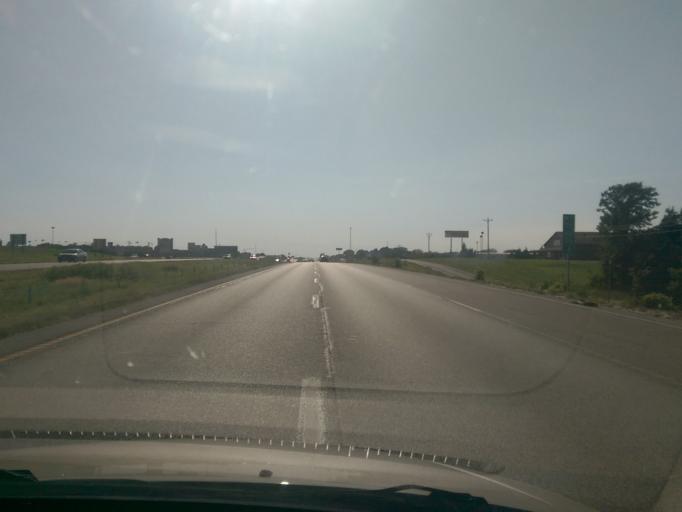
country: US
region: Missouri
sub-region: Lafayette County
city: Odessa
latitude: 39.0087
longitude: -93.9688
